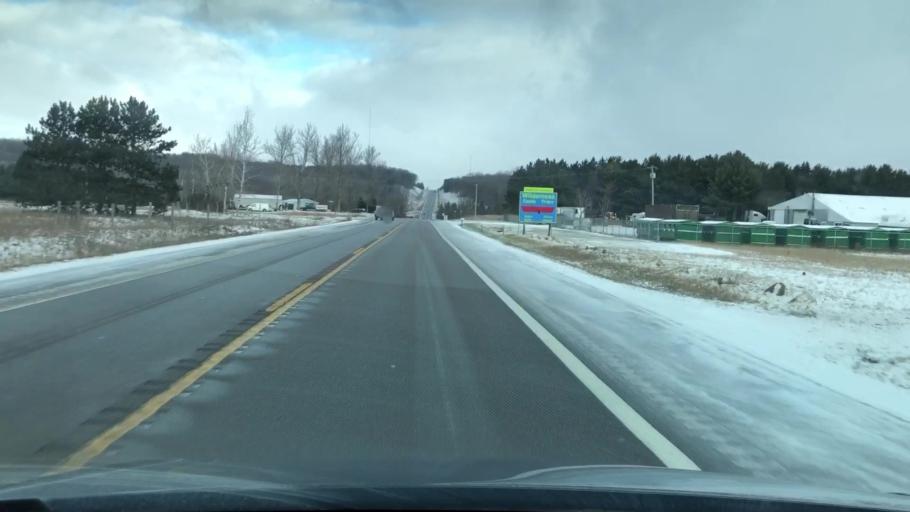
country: US
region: Michigan
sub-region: Grand Traverse County
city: Kingsley
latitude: 44.4312
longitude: -85.6985
